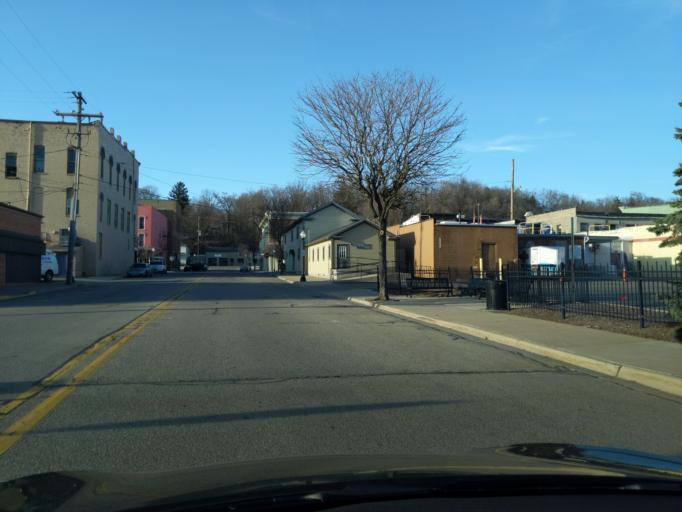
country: US
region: Michigan
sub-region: Ionia County
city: Ionia
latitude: 42.9815
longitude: -85.0678
